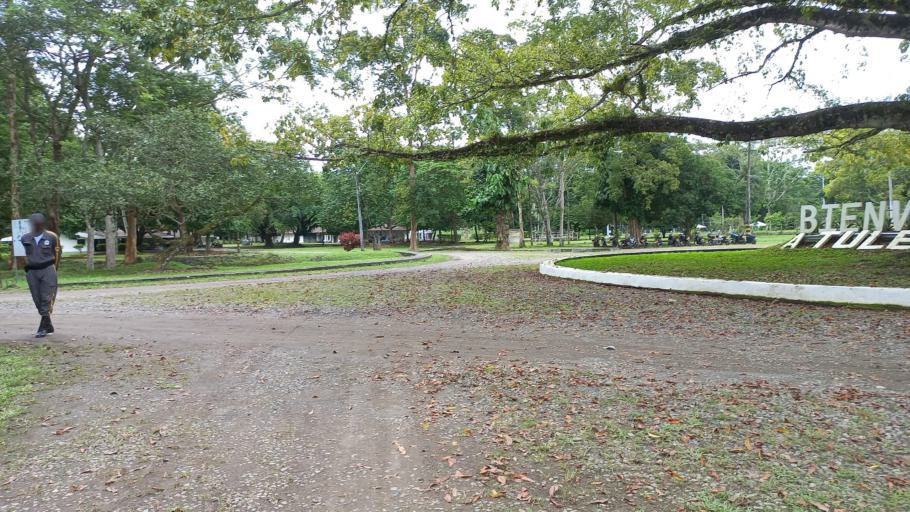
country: CO
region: Antioquia
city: Carepa
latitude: 7.7735
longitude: -76.6635
